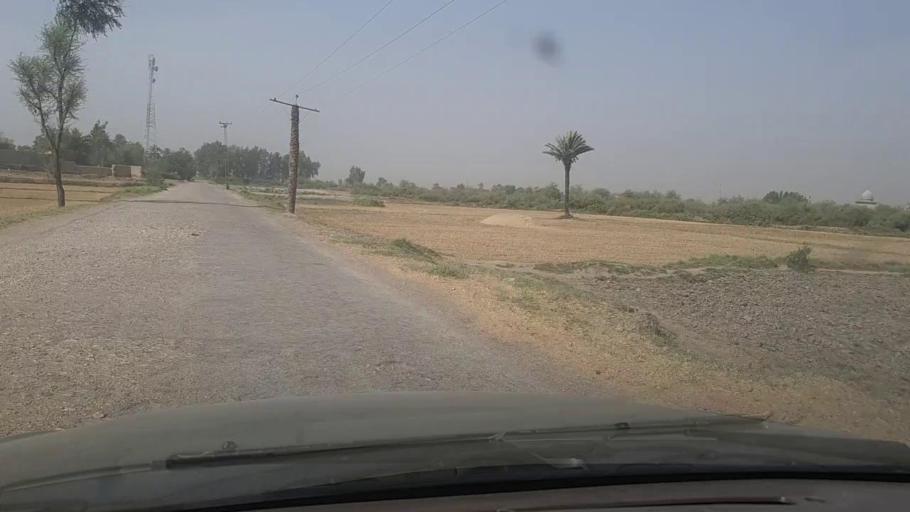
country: PK
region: Sindh
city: Garhi Yasin
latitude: 27.8635
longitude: 68.5512
